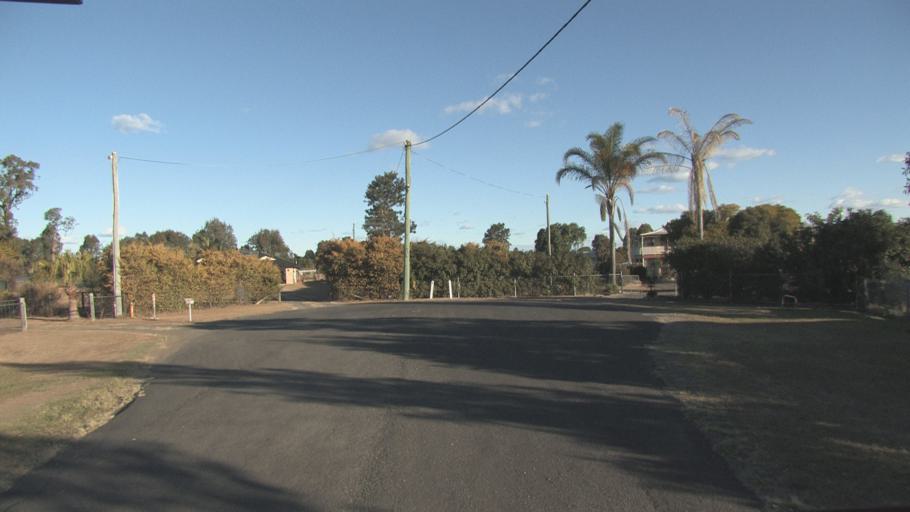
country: AU
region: Queensland
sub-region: Logan
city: Cedar Vale
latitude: -27.8656
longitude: 152.9660
